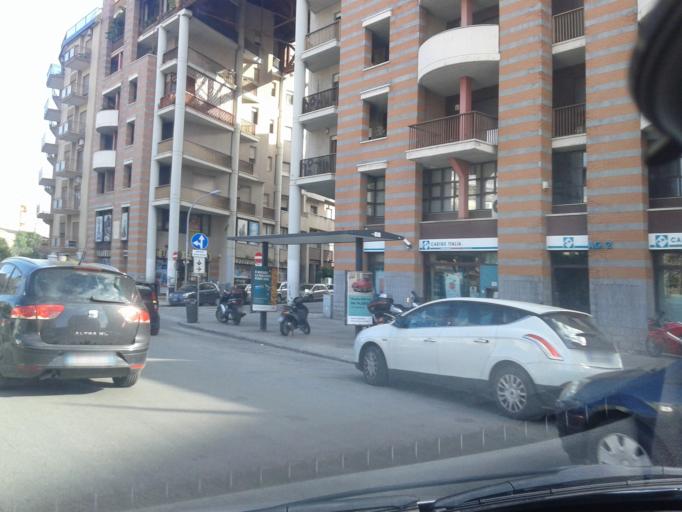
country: IT
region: Sicily
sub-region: Palermo
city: Palermo
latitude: 38.1198
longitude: 13.3398
